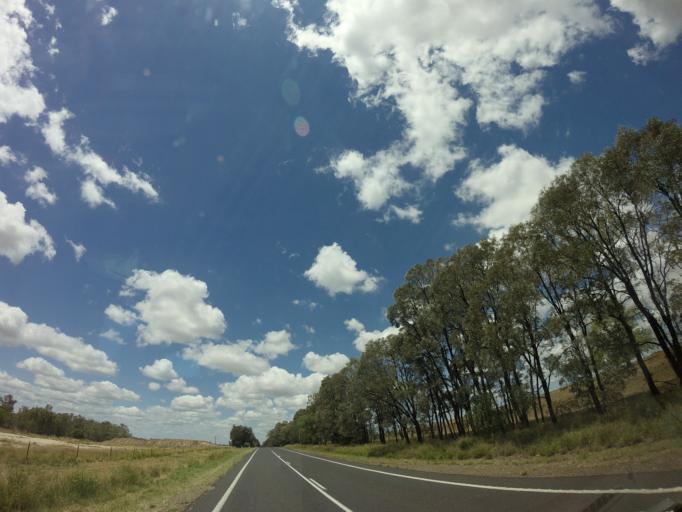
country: AU
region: Queensland
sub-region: Toowoomba
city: Oakey
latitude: -27.8961
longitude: 151.2057
